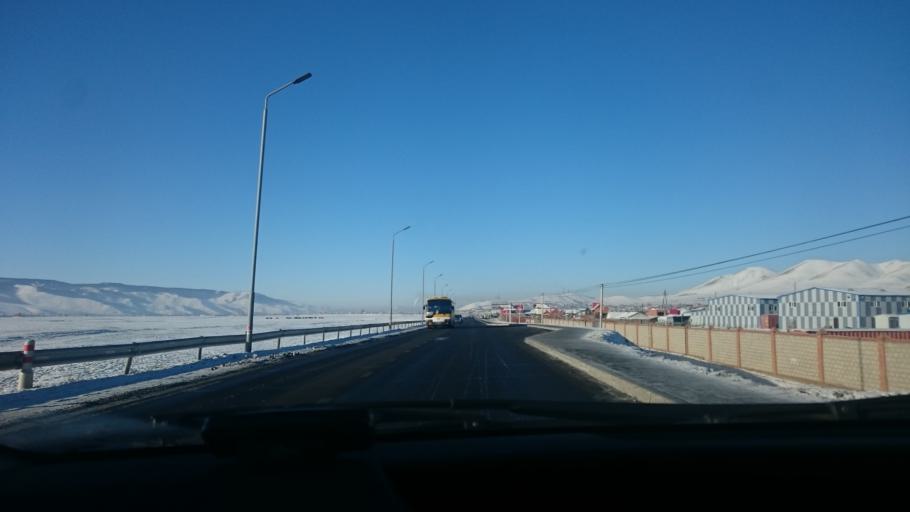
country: MN
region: Ulaanbaatar
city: Ulaanbaatar
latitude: 47.9158
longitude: 107.0844
